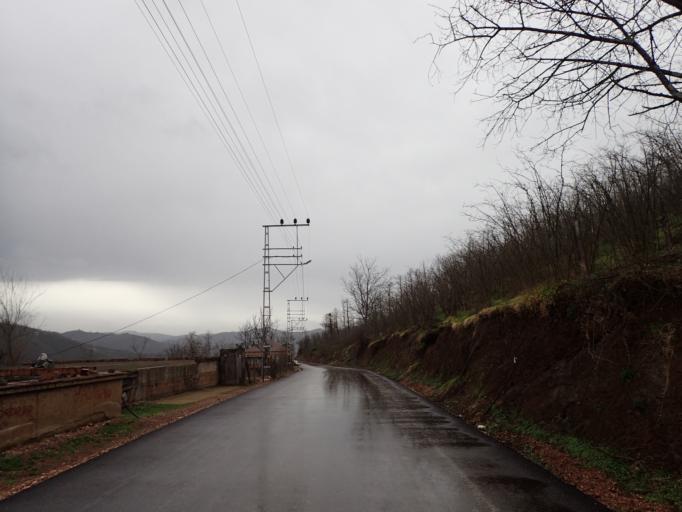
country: TR
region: Ordu
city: Camas
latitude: 40.8806
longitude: 37.4991
